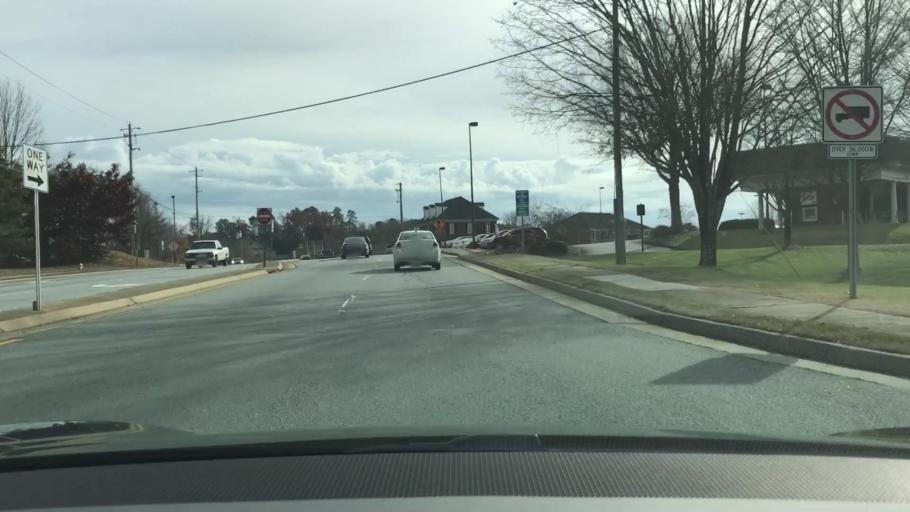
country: US
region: Georgia
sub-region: Gwinnett County
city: Buford
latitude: 34.1055
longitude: -84.0032
